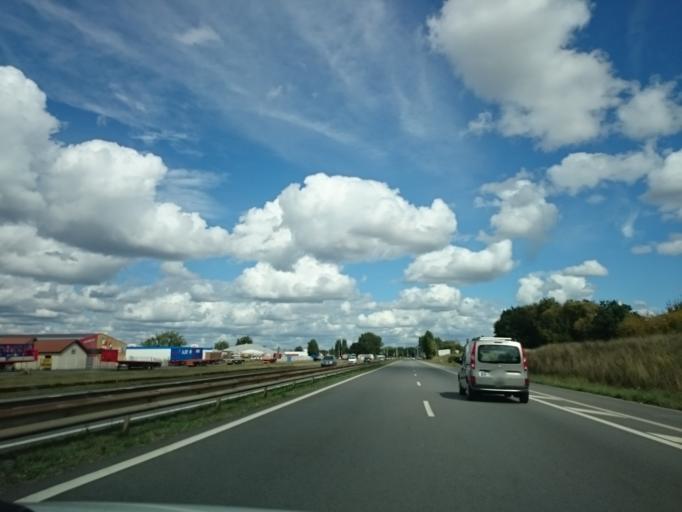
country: FR
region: Pays de la Loire
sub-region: Departement de la Loire-Atlantique
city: Bouguenais
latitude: 47.1870
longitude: -1.5950
